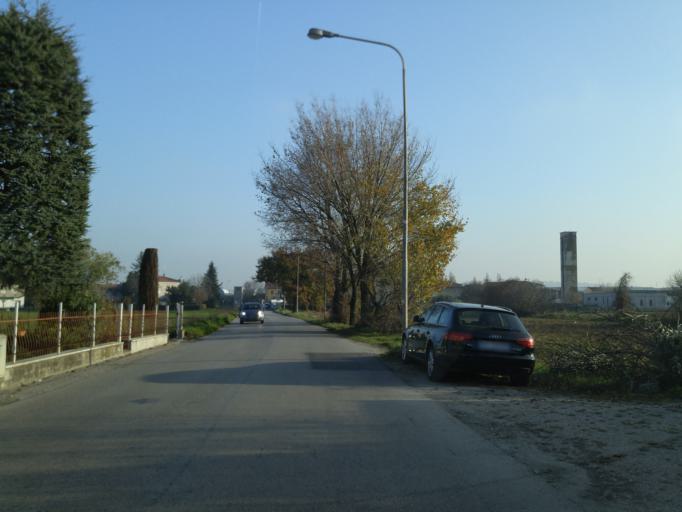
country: IT
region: The Marches
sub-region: Provincia di Pesaro e Urbino
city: Bellocchi
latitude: 43.7959
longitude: 12.9996
